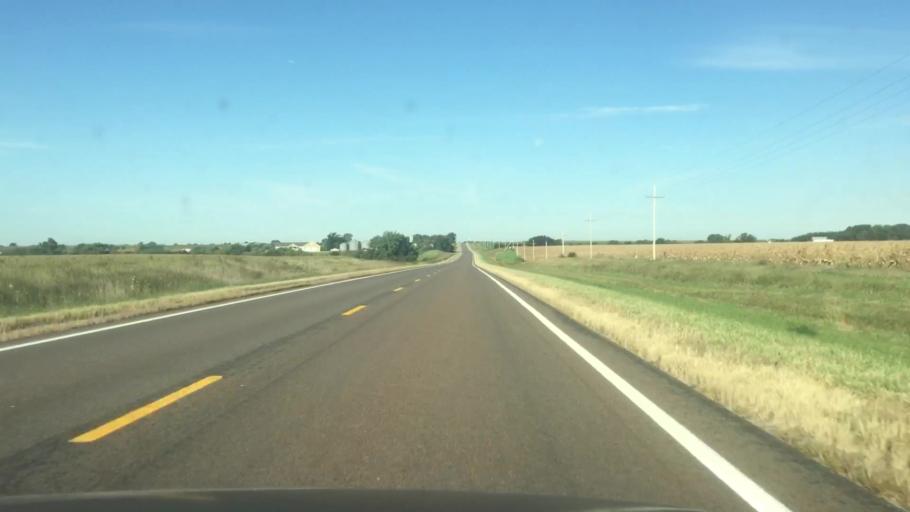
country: US
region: Nebraska
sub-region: Jefferson County
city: Fairbury
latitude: 40.1472
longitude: -97.3511
